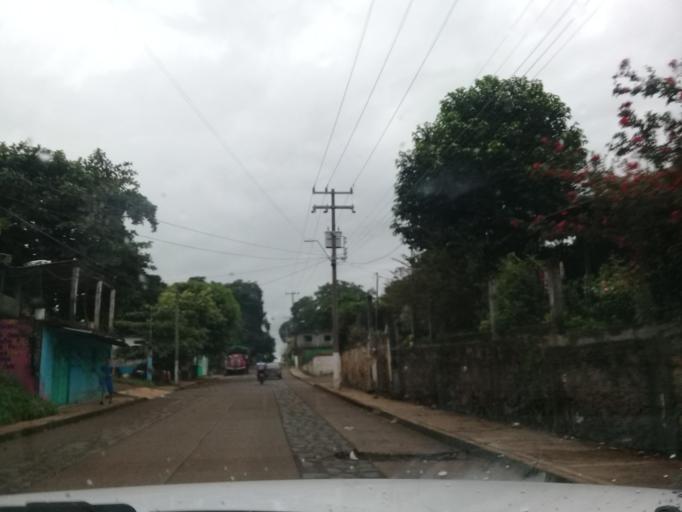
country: MX
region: Veracruz
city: San Andres Tuxtla
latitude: 18.4395
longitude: -95.2214
